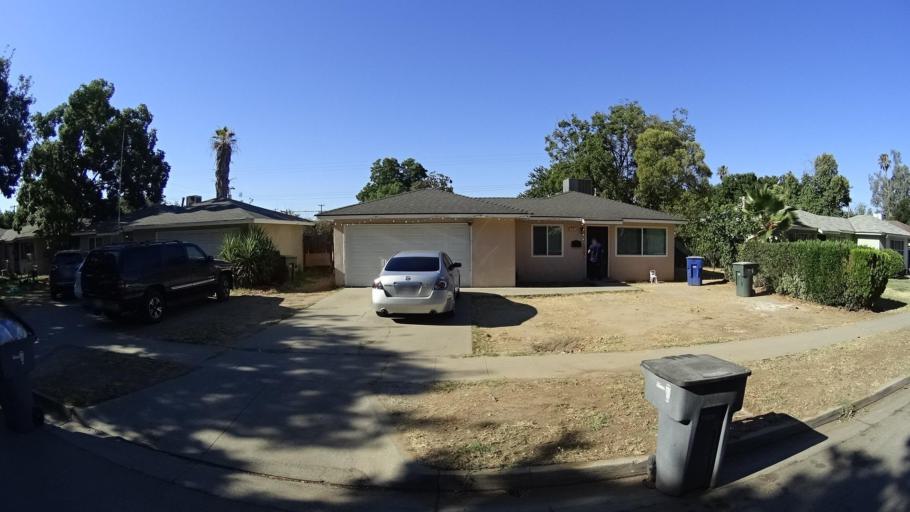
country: US
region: California
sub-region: Fresno County
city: Fresno
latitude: 36.7050
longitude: -119.7961
